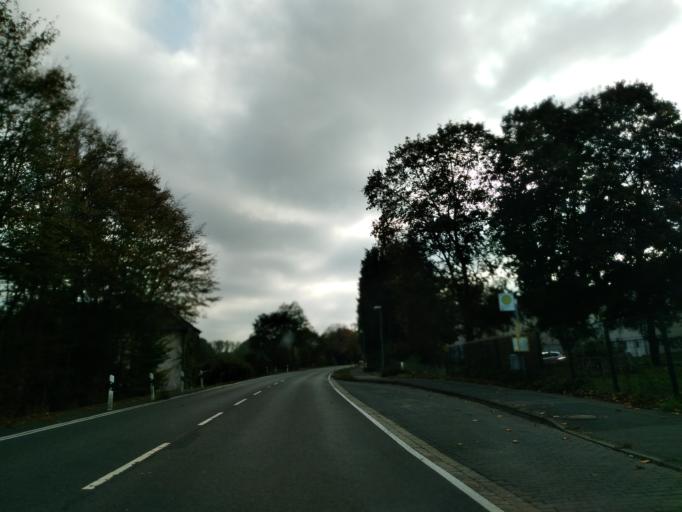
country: DE
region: North Rhine-Westphalia
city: Sankt Augustin
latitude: 50.7626
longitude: 7.2153
